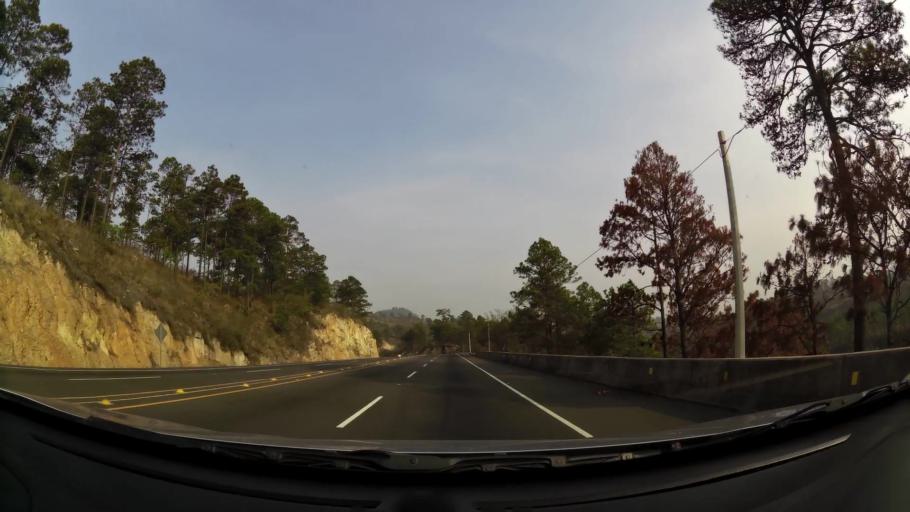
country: HN
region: Francisco Morazan
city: Zambrano
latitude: 14.2552
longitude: -87.3864
